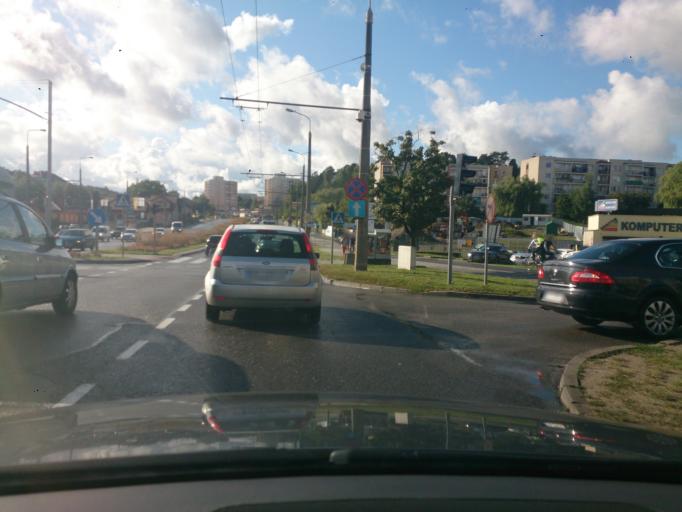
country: PL
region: Pomeranian Voivodeship
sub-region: Gdynia
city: Wielki Kack
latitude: 54.4701
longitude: 18.4970
